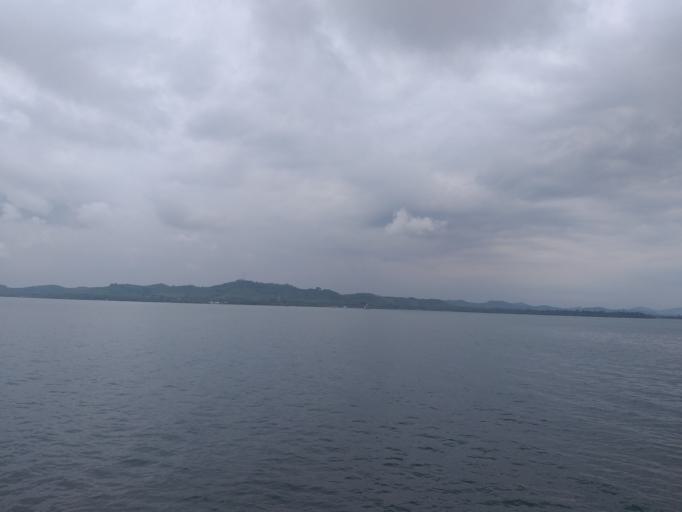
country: TH
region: Trat
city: Laem Ngop
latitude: 12.1624
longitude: 102.2925
